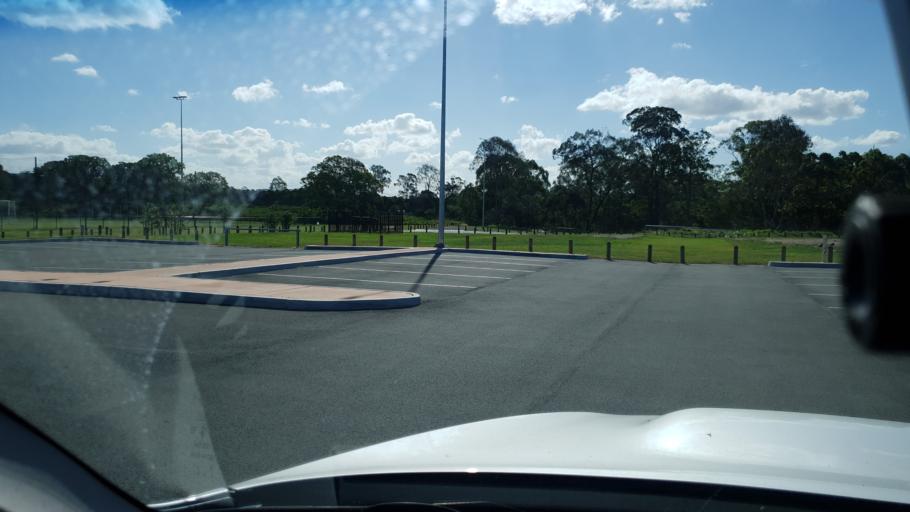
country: AU
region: Queensland
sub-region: Logan
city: Woodridge
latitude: -27.6710
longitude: 153.0683
